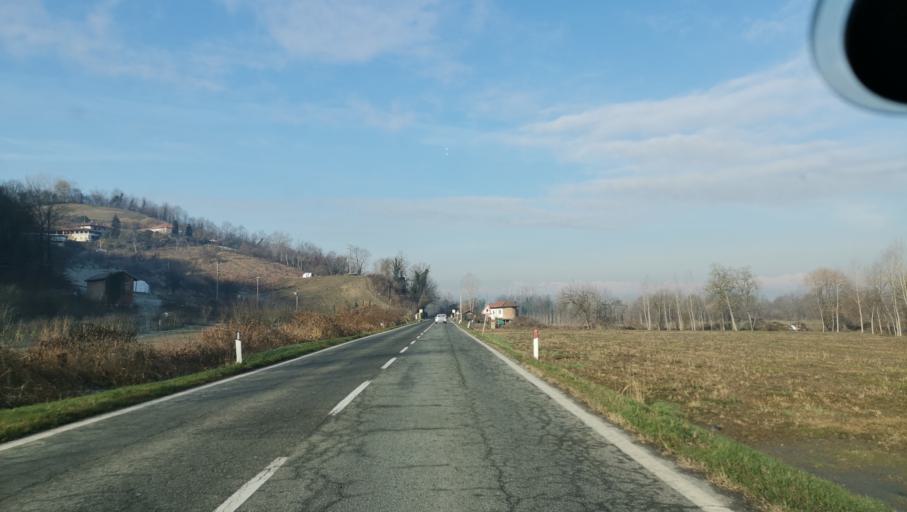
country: IT
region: Piedmont
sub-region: Provincia di Torino
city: Chivasso
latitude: 45.1742
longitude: 7.9228
